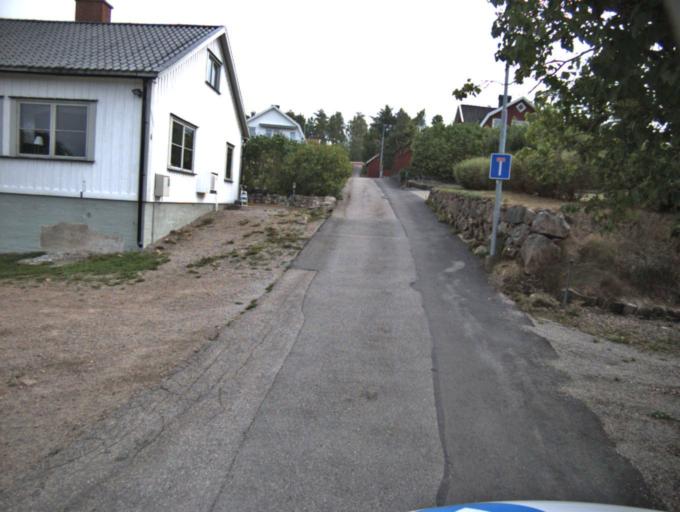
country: SE
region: Vaestra Goetaland
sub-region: Ulricehamns Kommun
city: Ulricehamn
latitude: 57.7398
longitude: 13.4219
